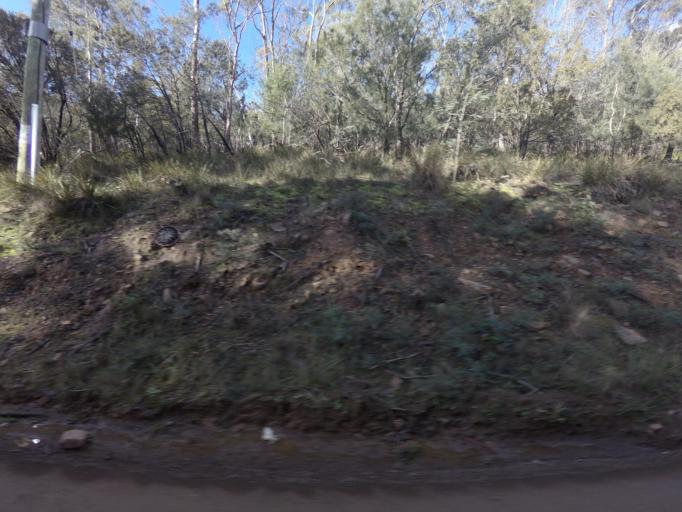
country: AU
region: Tasmania
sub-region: Derwent Valley
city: New Norfolk
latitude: -42.8159
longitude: 147.1292
